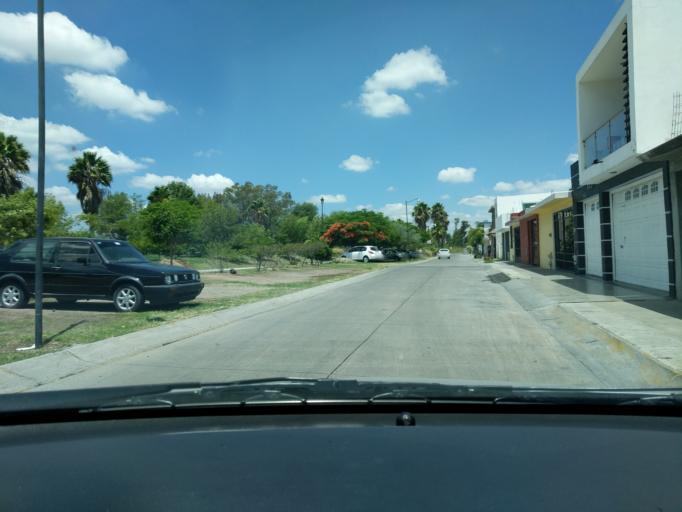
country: MX
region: Guanajuato
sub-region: Salamanca
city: El Divisador
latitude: 20.5983
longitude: -101.1703
